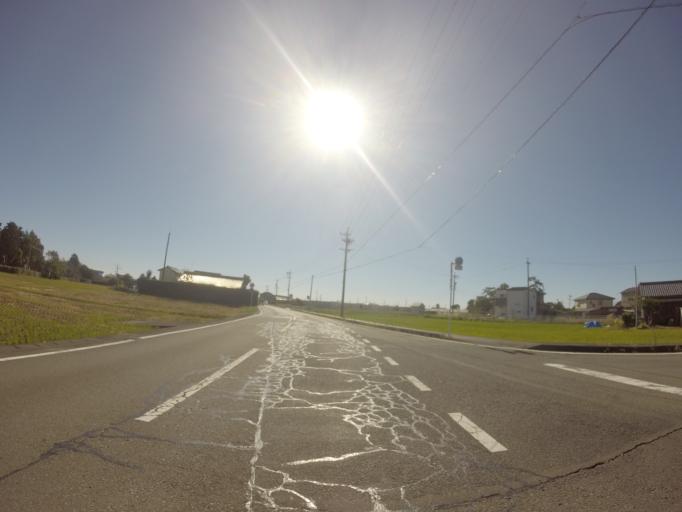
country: JP
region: Shizuoka
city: Fujieda
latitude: 34.8259
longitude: 138.2528
